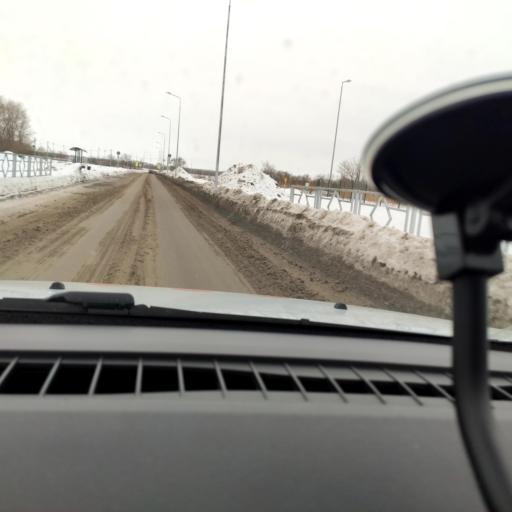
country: RU
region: Samara
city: Samara
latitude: 53.0908
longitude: 50.1592
